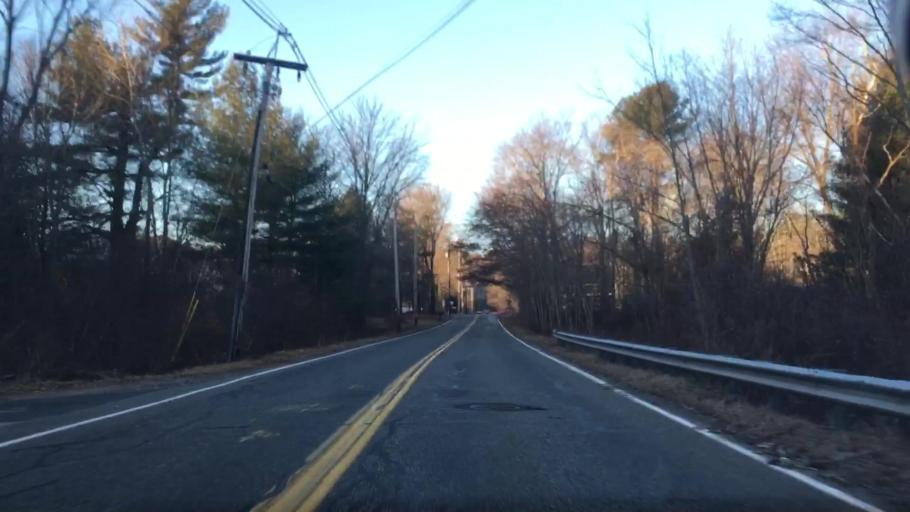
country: US
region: Massachusetts
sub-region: Hampden County
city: East Longmeadow
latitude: 42.0446
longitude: -72.4899
